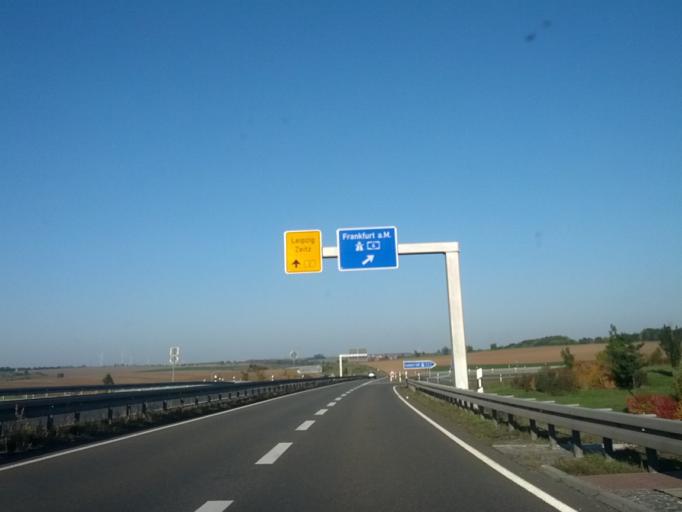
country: DE
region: Thuringia
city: Schwaara
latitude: 50.9032
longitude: 12.1267
